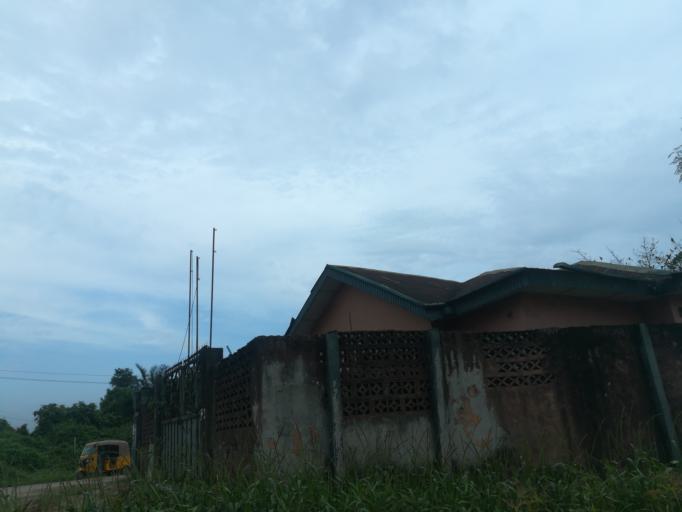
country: NG
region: Rivers
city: Port Harcourt
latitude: 4.7915
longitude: 6.9579
